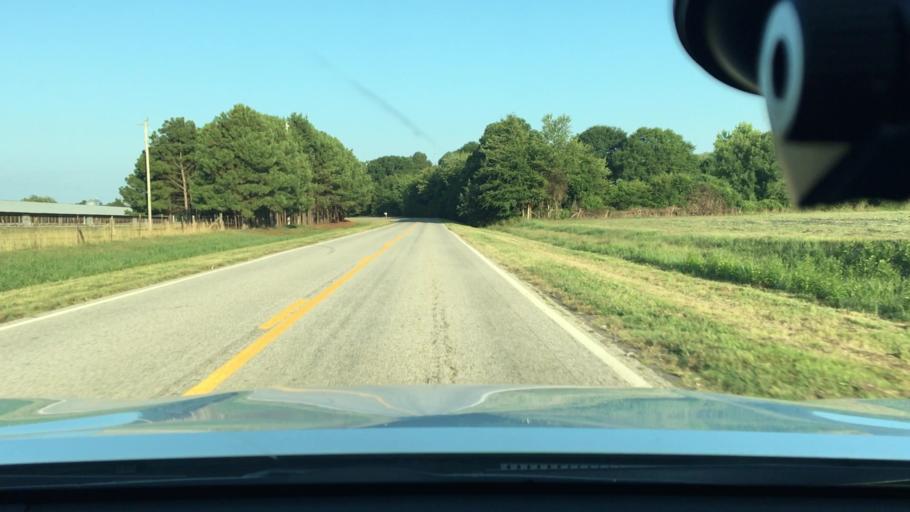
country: US
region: Arkansas
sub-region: Johnson County
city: Coal Hill
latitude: 35.3576
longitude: -93.5578
